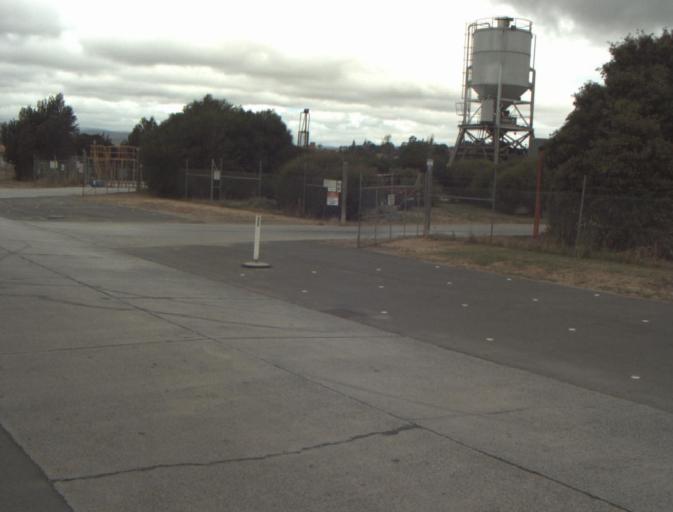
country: AU
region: Tasmania
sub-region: Launceston
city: Launceston
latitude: -41.4286
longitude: 147.1264
